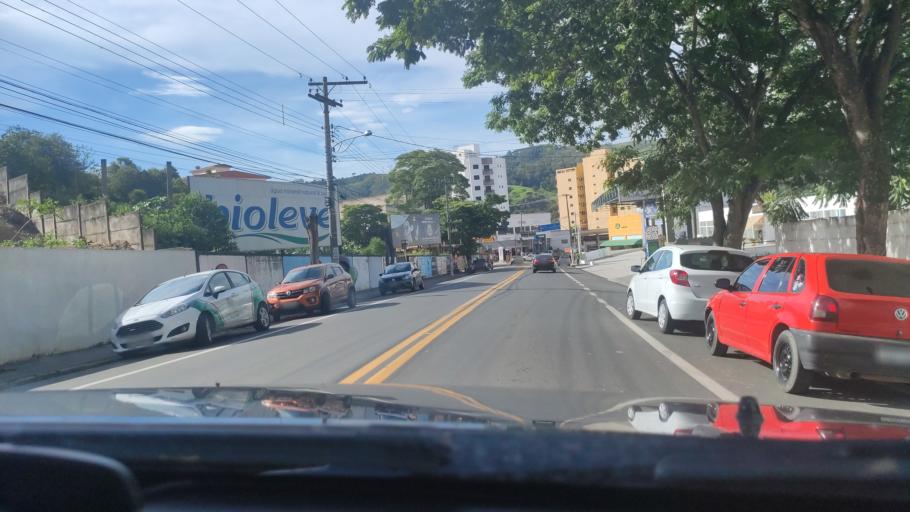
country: BR
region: Sao Paulo
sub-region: Aguas De Lindoia
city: Aguas de Lindoia
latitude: -22.5241
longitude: -46.6476
